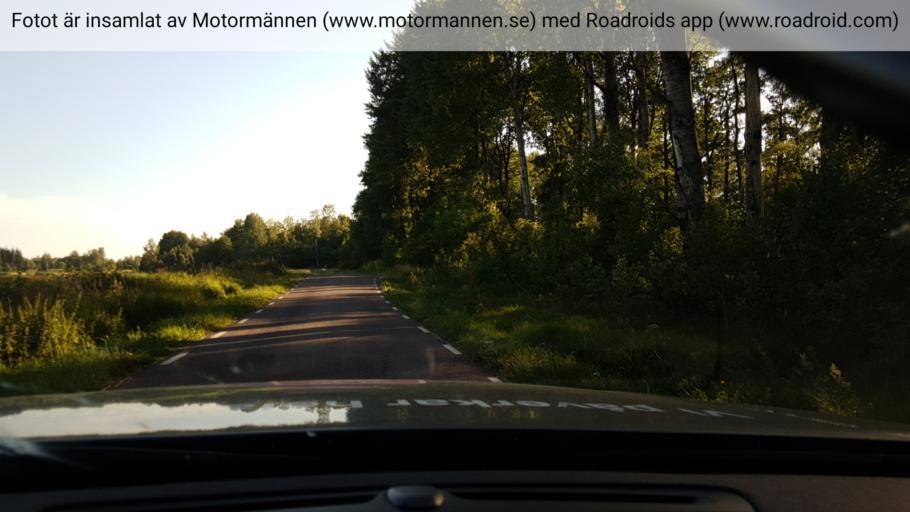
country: SE
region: Vaestmanland
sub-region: Surahammars Kommun
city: Surahammar
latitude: 59.6811
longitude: 16.0848
